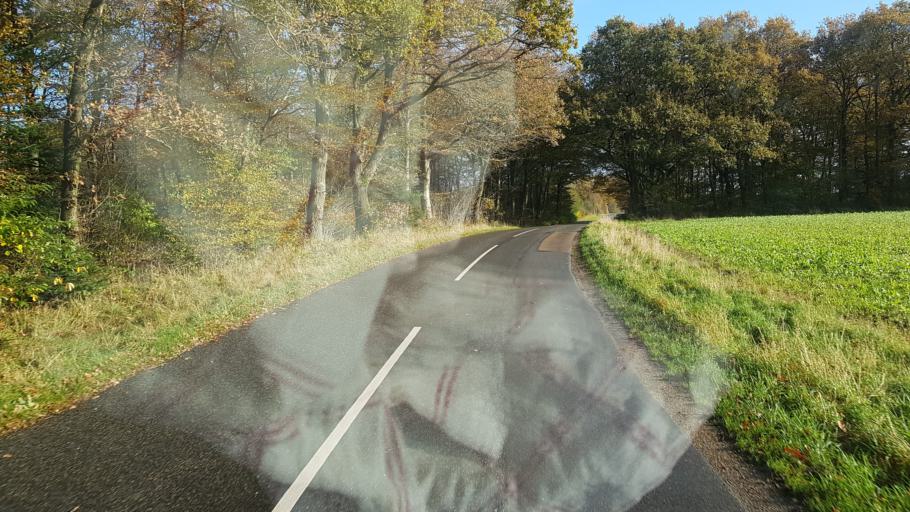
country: DK
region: South Denmark
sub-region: Varde Kommune
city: Olgod
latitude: 55.6907
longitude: 8.6650
